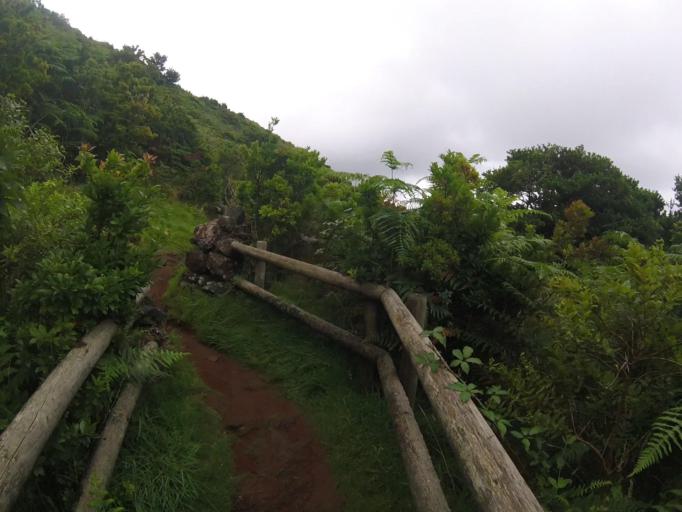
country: PT
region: Azores
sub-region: Praia da Vitoria
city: Biscoitos
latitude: 38.7297
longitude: -27.2311
